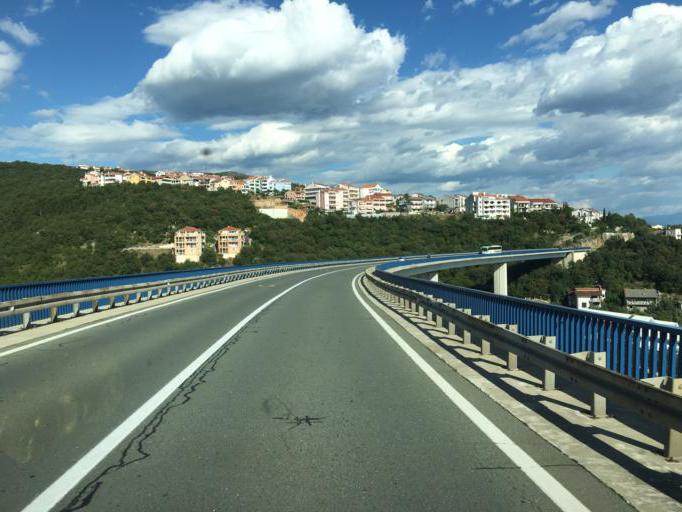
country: HR
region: Primorsko-Goranska
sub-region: Grad Crikvenica
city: Crikvenica
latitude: 45.1764
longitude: 14.6934
